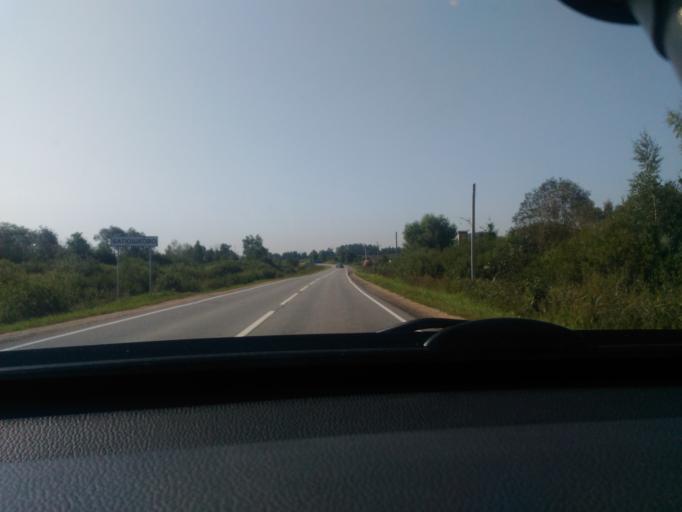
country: RU
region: Moskovskaya
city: Podosinki
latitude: 56.2295
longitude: 37.5494
